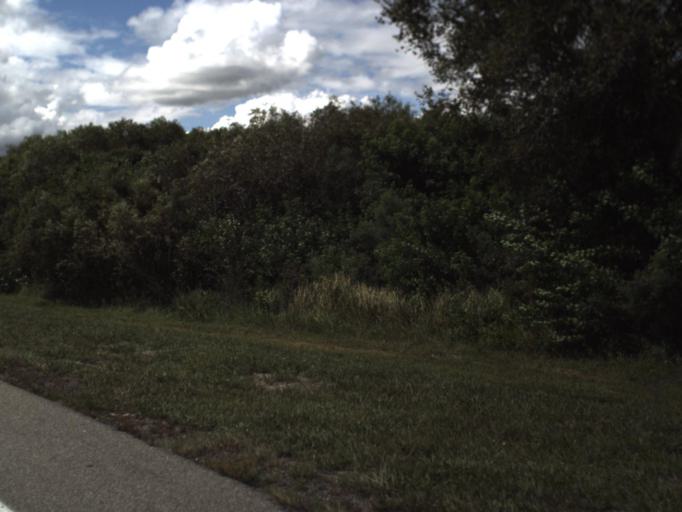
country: US
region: Florida
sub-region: Polk County
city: Mulberry
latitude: 27.7448
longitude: -81.9971
